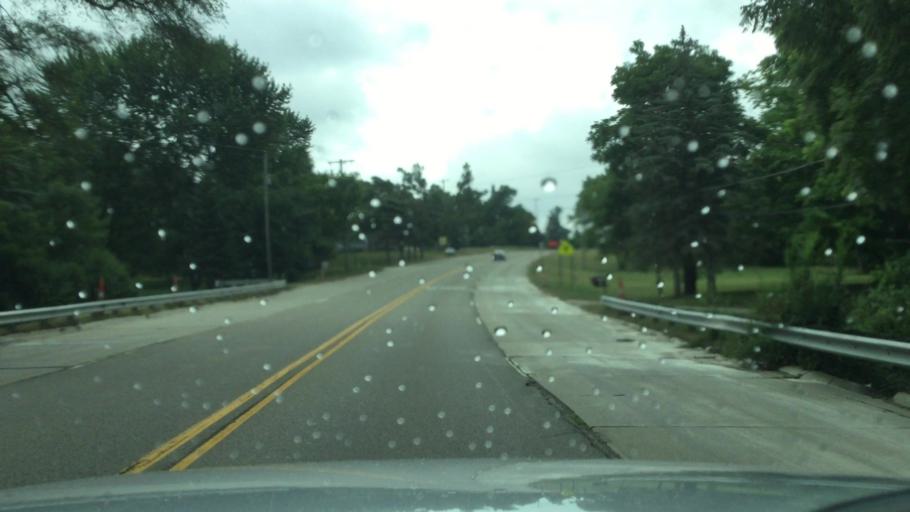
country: US
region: Michigan
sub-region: Genesee County
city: Flint
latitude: 43.0274
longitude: -83.7592
